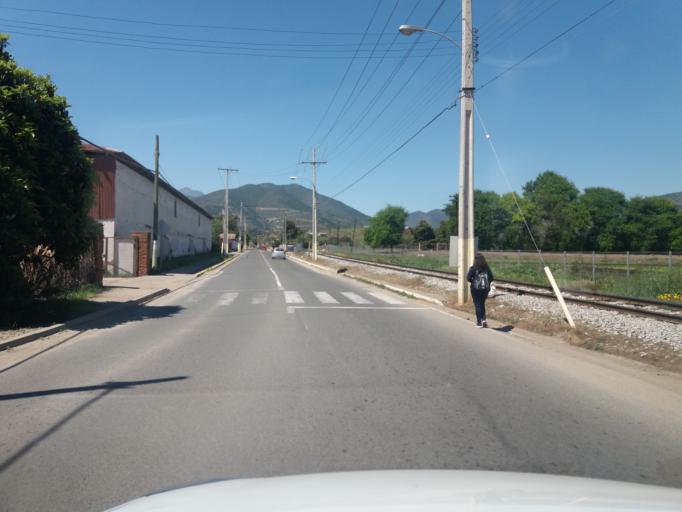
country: CL
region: Valparaiso
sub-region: Provincia de Quillota
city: Quillota
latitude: -32.9392
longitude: -71.2859
